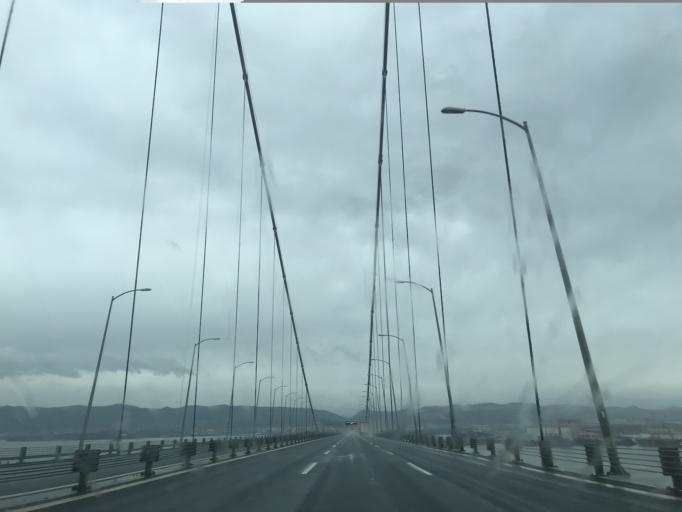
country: TR
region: Yalova
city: Altinova
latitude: 40.7469
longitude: 29.5145
